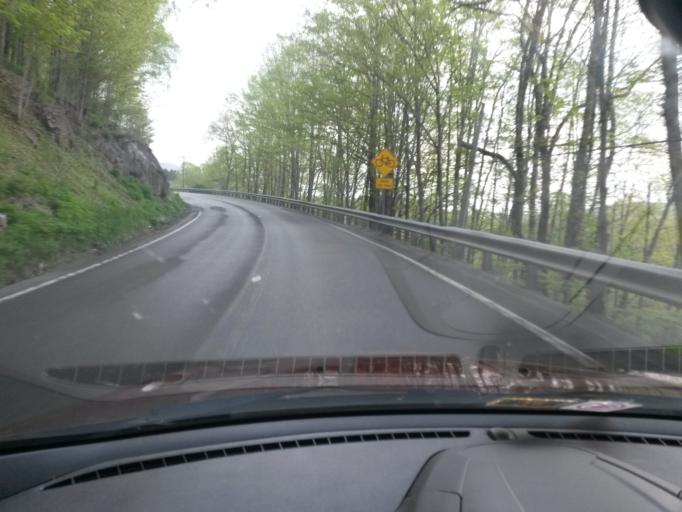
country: US
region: Virginia
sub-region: Highland County
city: Monterey
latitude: 38.5810
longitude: -79.8414
